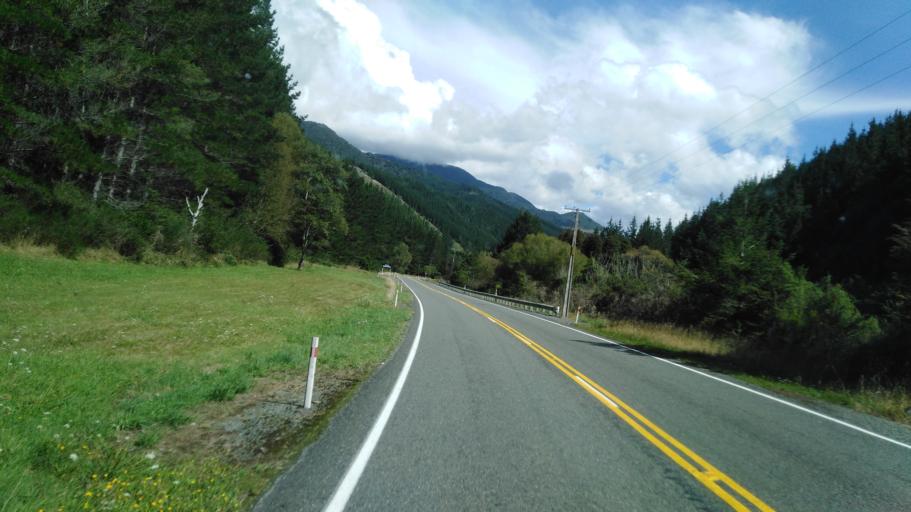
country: NZ
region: Nelson
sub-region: Nelson City
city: Nelson
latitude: -41.1669
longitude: 173.5132
